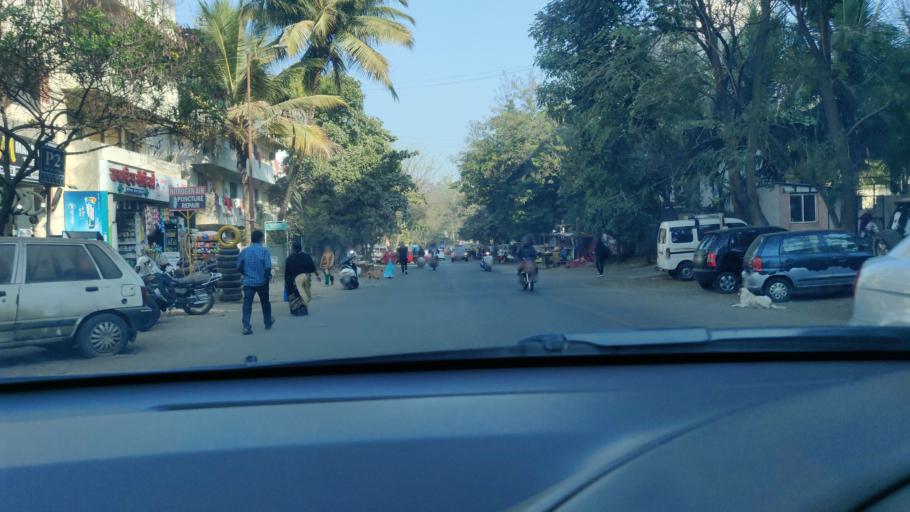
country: IN
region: Maharashtra
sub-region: Pune Division
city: Khadki
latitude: 18.5641
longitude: 73.8026
